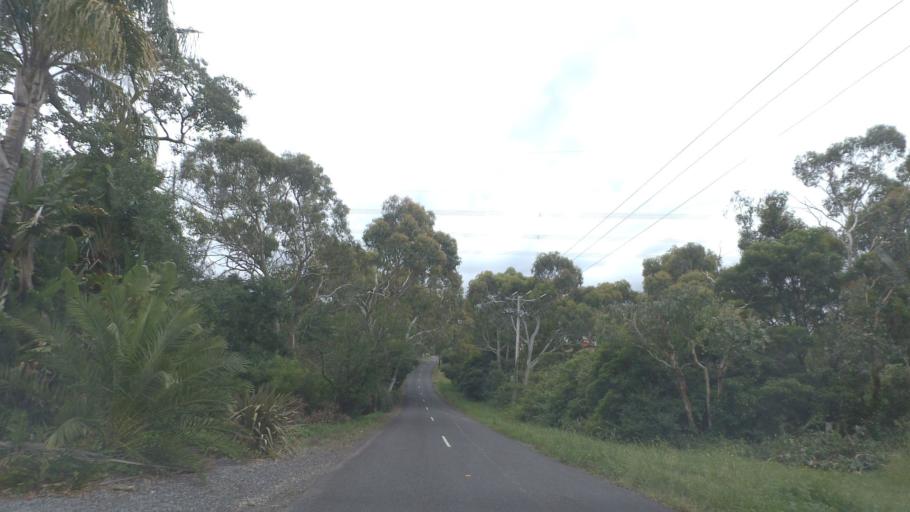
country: AU
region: Victoria
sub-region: Manningham
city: Warrandyte
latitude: -37.7651
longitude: 145.2338
